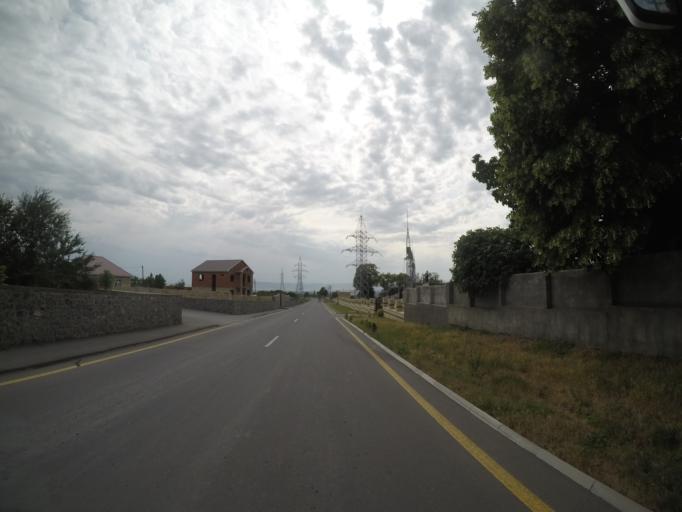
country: AZ
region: Qakh Rayon
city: Qax
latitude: 41.4141
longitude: 46.9025
